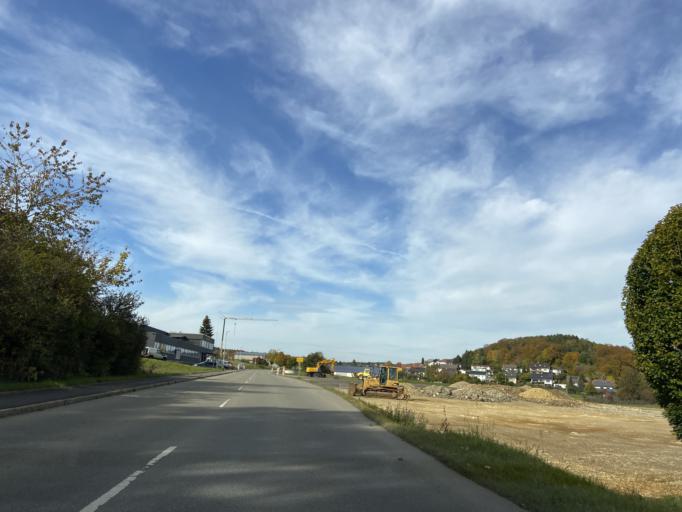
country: DE
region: Baden-Wuerttemberg
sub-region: Tuebingen Region
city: Schwenningen
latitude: 48.1049
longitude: 9.0078
